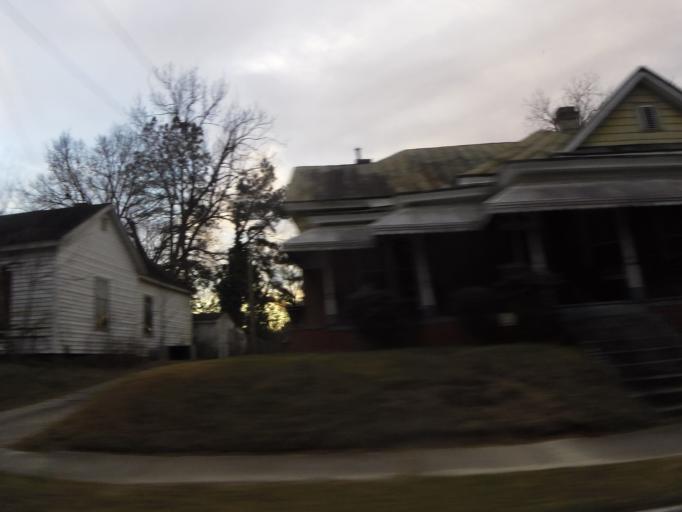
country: US
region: North Carolina
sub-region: Nash County
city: Rocky Mount
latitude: 35.9468
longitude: -77.8041
